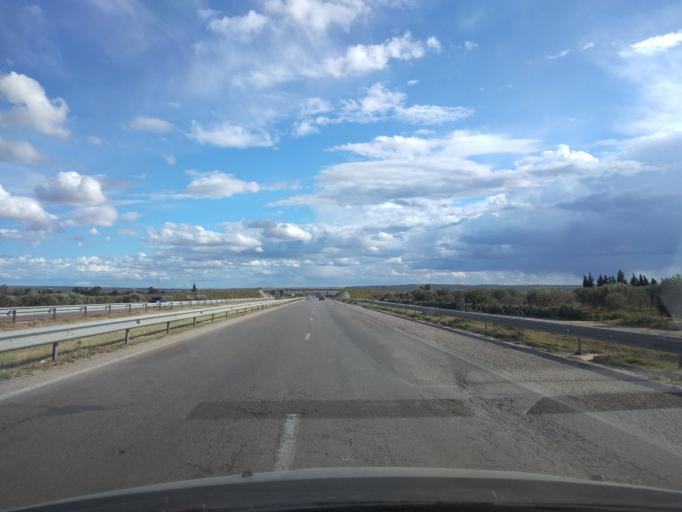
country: TN
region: Al Munastir
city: Manzil Kamil
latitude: 35.5946
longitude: 10.6032
